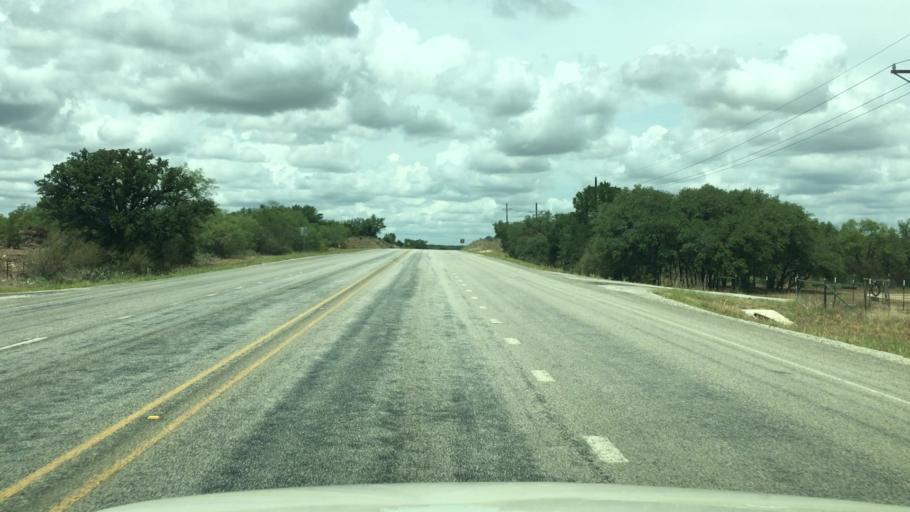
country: US
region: Texas
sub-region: McCulloch County
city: Brady
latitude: 31.0081
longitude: -99.2052
